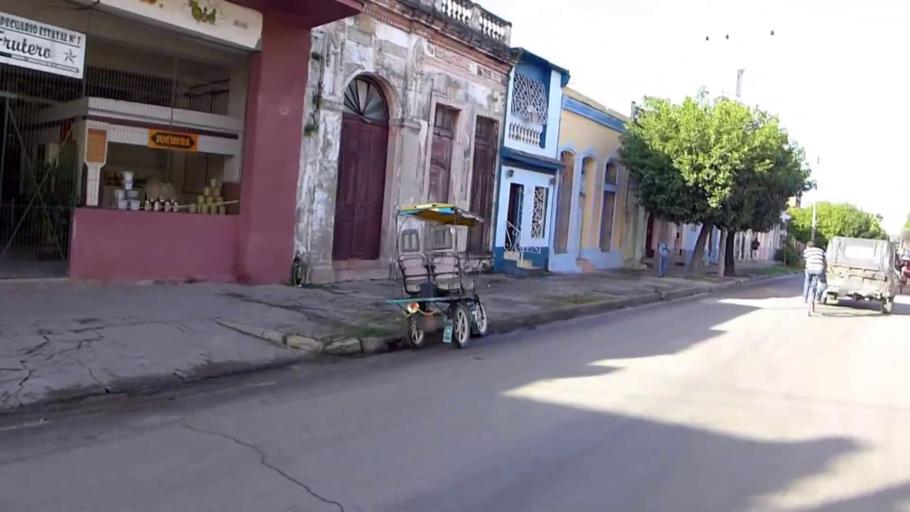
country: CU
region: Camaguey
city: Camaguey
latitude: 21.3849
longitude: -77.9265
